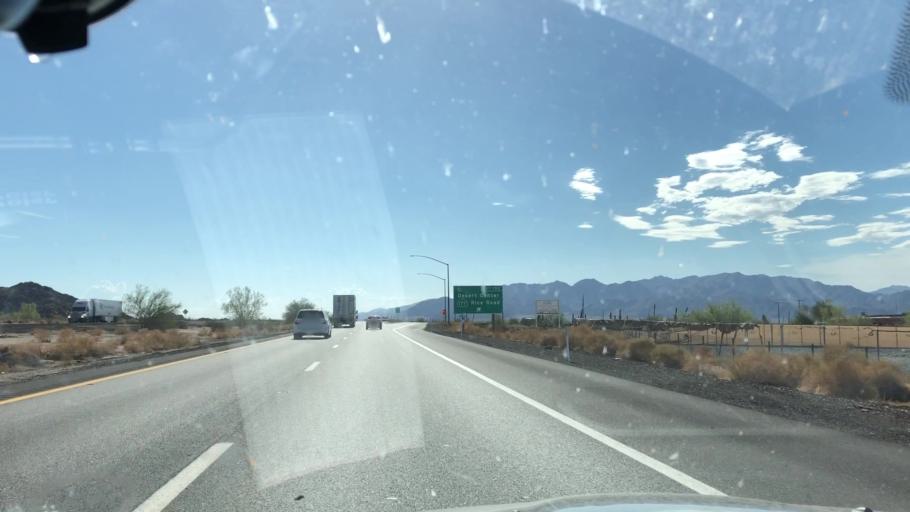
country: US
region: California
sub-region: Imperial County
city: Niland
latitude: 33.7108
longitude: -115.3955
